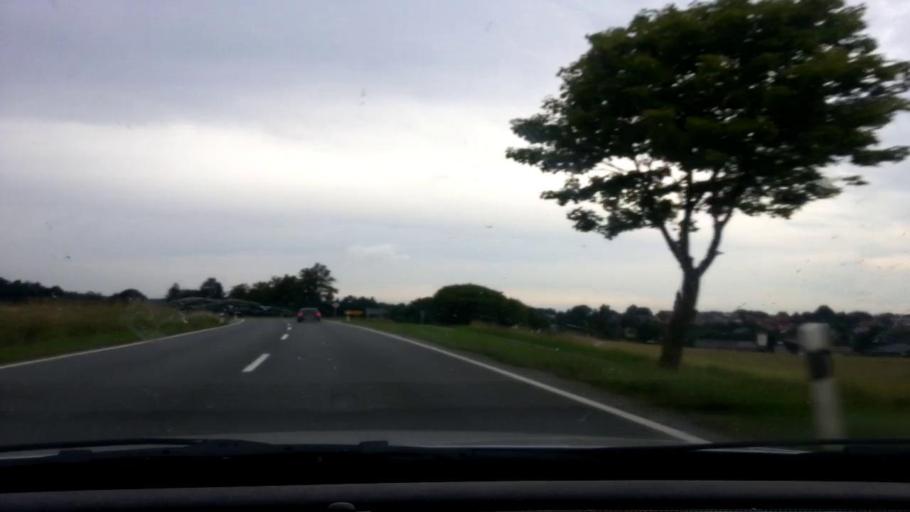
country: DE
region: Bavaria
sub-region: Upper Franconia
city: Neunkirchen am Main
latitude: 49.9167
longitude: 11.6514
